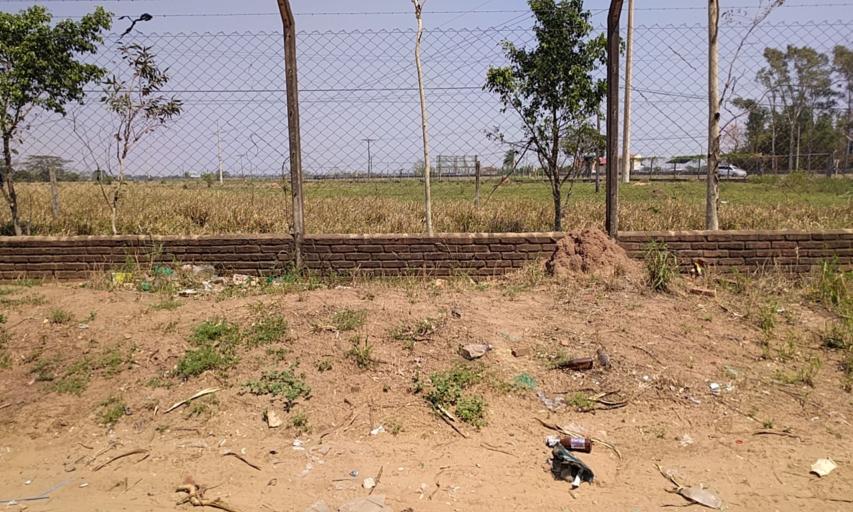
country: BO
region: Santa Cruz
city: Warnes
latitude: -17.4490
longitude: -63.1892
